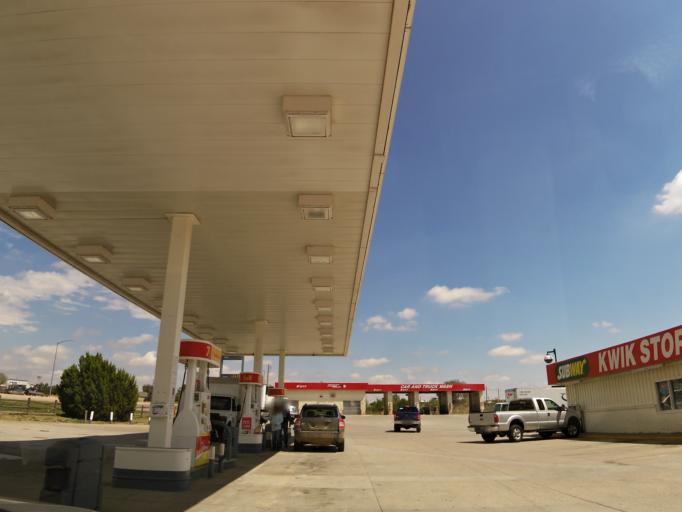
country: US
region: Colorado
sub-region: Fremont County
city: Penrose
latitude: 38.4226
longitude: -105.0328
